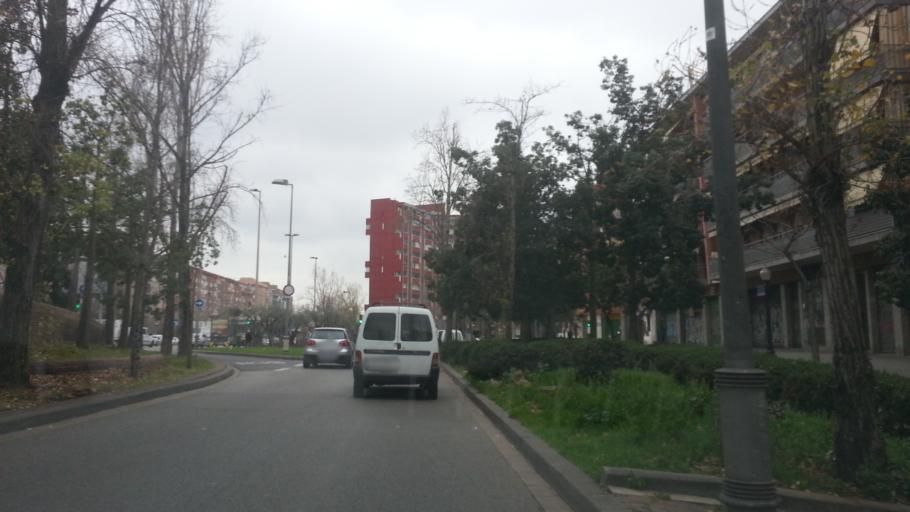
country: ES
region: Catalonia
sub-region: Provincia de Barcelona
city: Sant Andreu de Palomar
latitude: 41.4435
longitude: 2.1861
